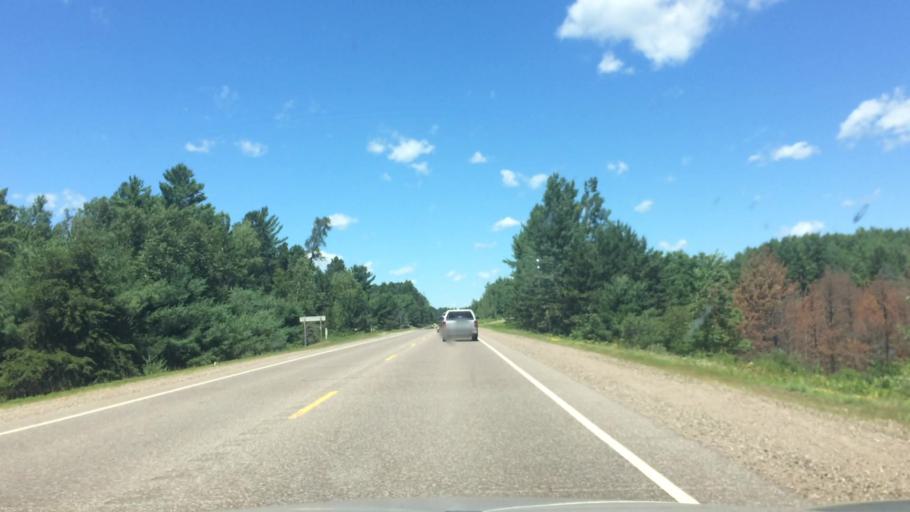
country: US
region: Wisconsin
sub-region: Lincoln County
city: Tomahawk
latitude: 45.6461
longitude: -89.7049
